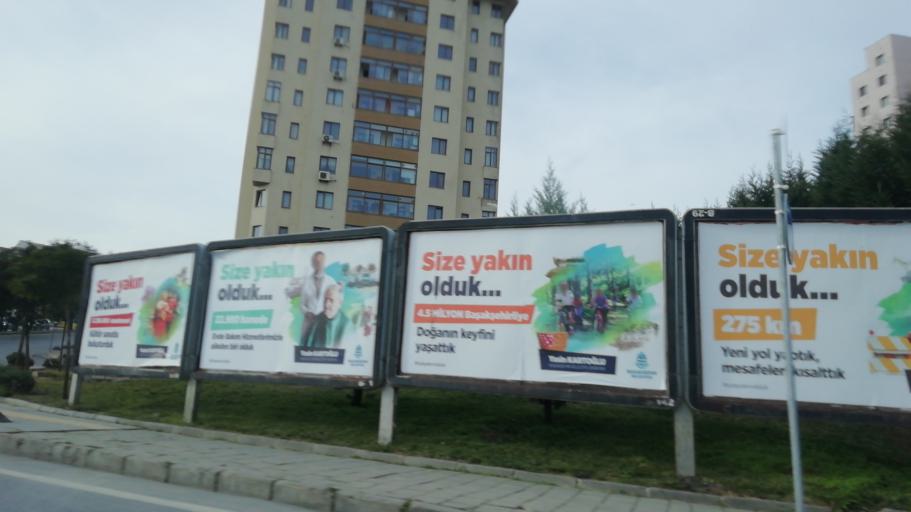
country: TR
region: Istanbul
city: Basaksehir
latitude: 41.1078
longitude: 28.7950
